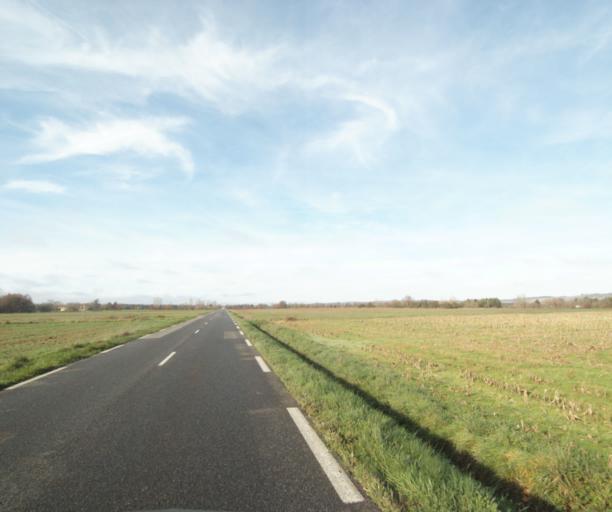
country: FR
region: Midi-Pyrenees
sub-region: Departement du Tarn-et-Garonne
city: Nohic
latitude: 43.8780
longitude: 1.4540
